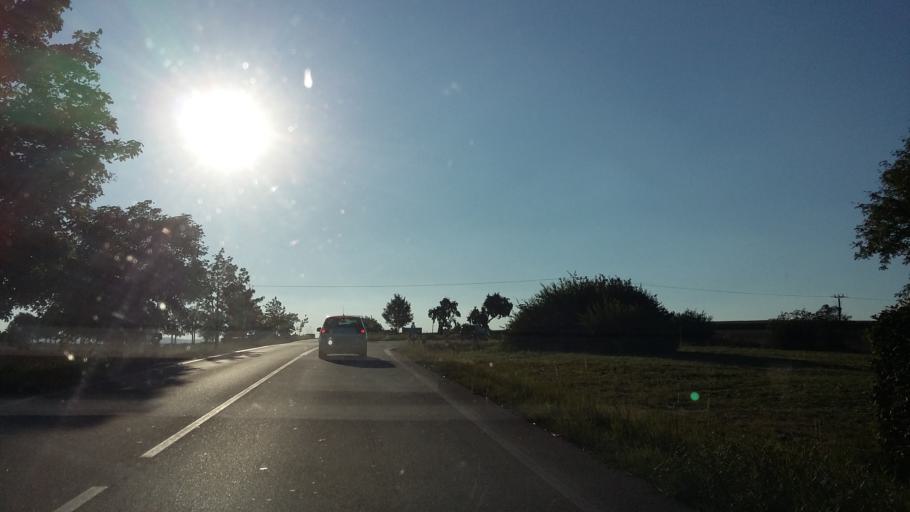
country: CZ
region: Vysocina
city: Velky Beranov
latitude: 49.4027
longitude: 15.6623
